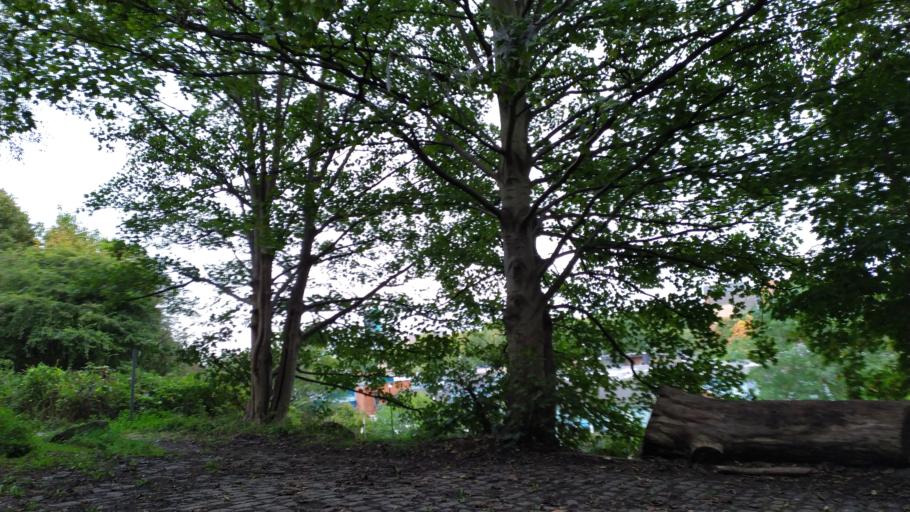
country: GB
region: England
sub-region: City and Borough of Leeds
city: Chapel Allerton
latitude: 53.8164
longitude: -1.5436
